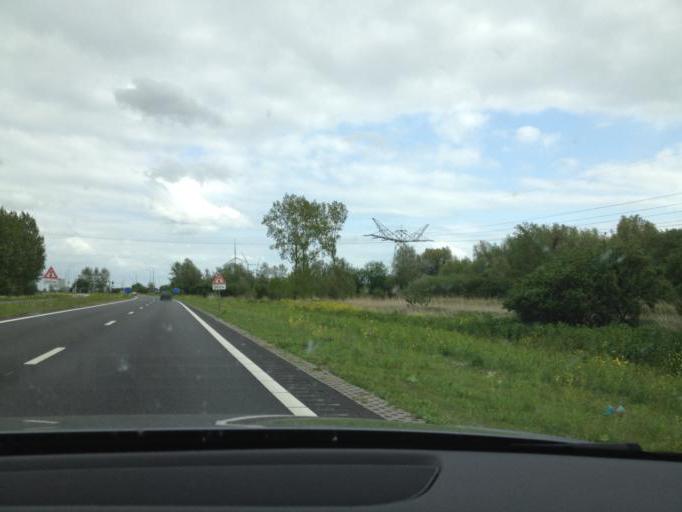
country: NL
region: Utrecht
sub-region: Gemeente Bunschoten
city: Spakenburg
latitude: 52.3106
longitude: 5.3416
